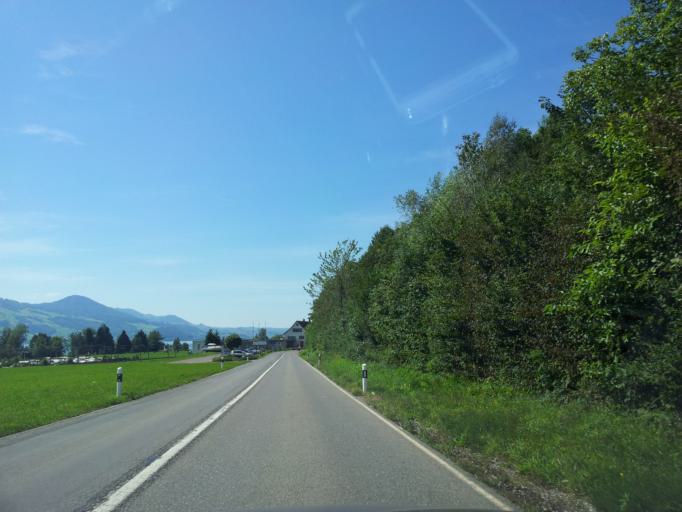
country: CH
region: Schwyz
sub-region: Bezirk March
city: Lachen
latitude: 47.2180
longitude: 8.8852
